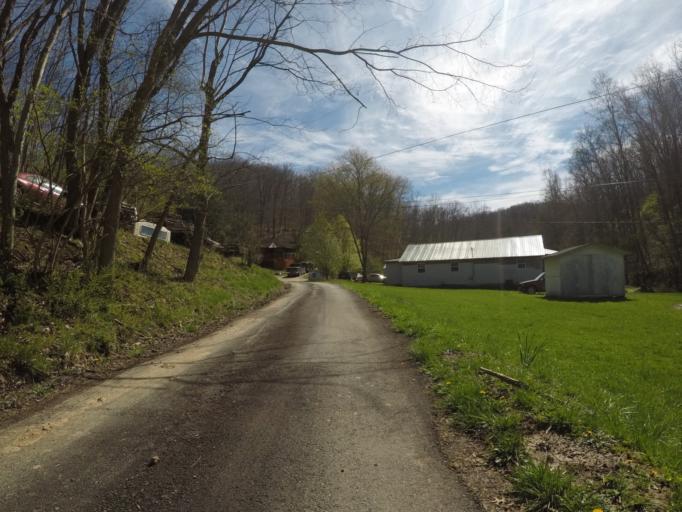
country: US
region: West Virginia
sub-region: Cabell County
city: Pea Ridge
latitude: 38.3993
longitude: -82.3472
